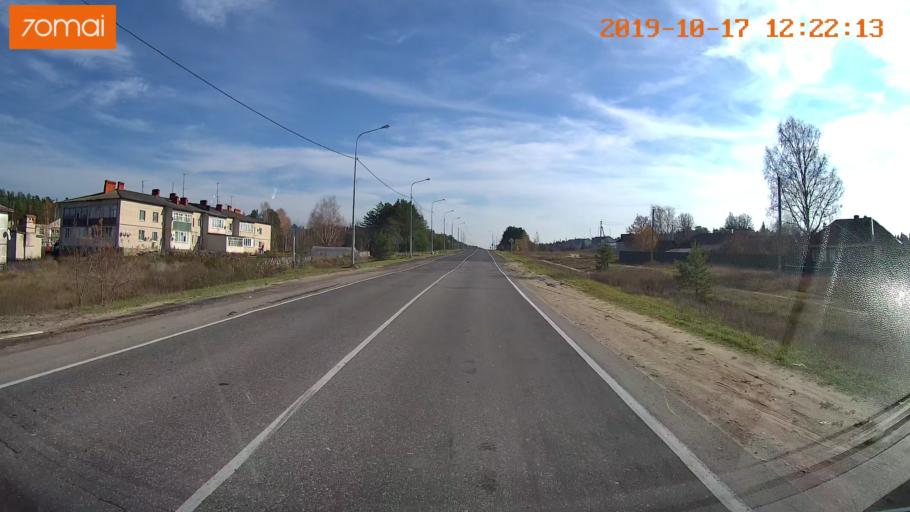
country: RU
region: Rjazan
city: Gus'-Zheleznyy
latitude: 55.0533
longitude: 41.1682
